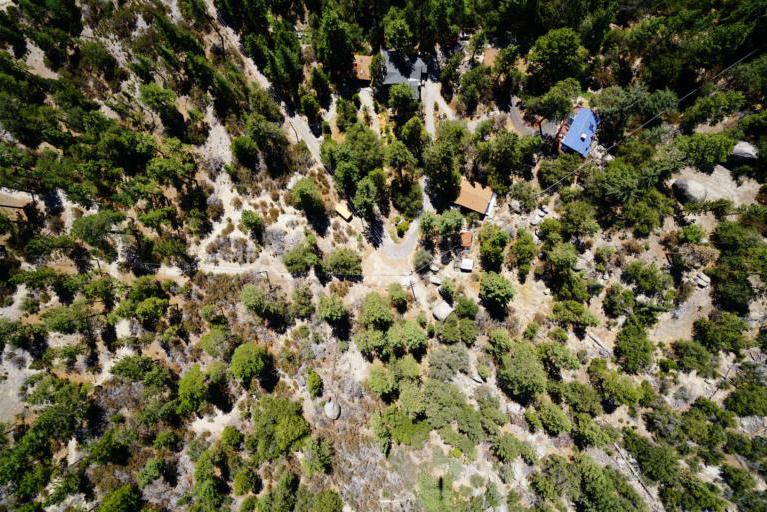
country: US
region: California
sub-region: Riverside County
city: Idyllwild-Pine Cove
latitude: 33.7551
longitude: -116.7244
